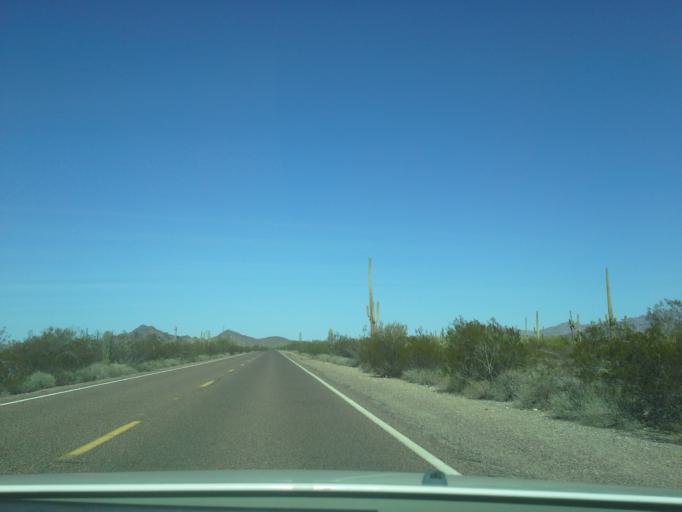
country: MX
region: Sonora
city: Sonoyta
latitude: 31.8964
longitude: -112.8118
